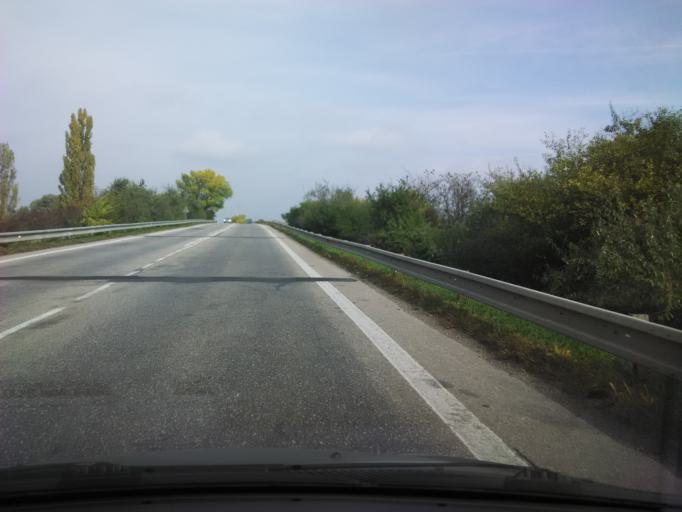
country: SK
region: Nitriansky
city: Komarno
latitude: 47.7750
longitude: 18.1591
